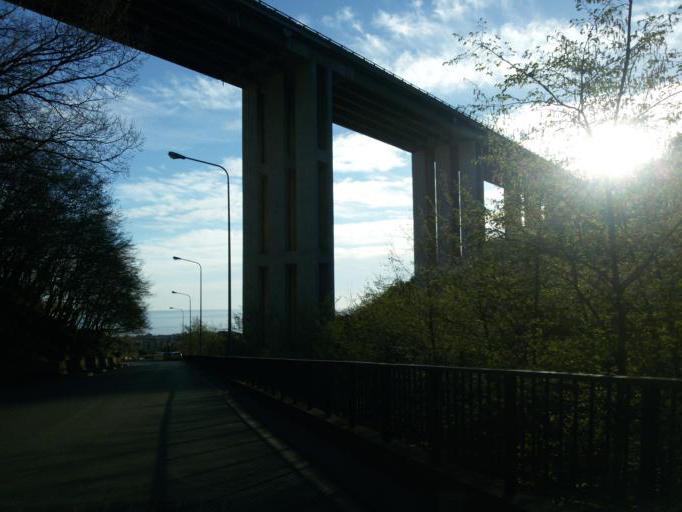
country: IT
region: Liguria
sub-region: Provincia di Genova
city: Bogliasco
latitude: 44.3960
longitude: 9.0142
